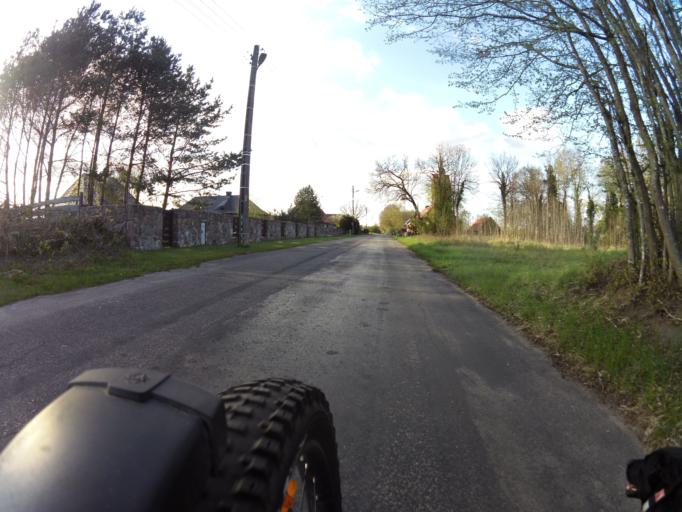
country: PL
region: West Pomeranian Voivodeship
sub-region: Powiat gryficki
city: Ploty
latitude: 53.7434
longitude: 15.2720
